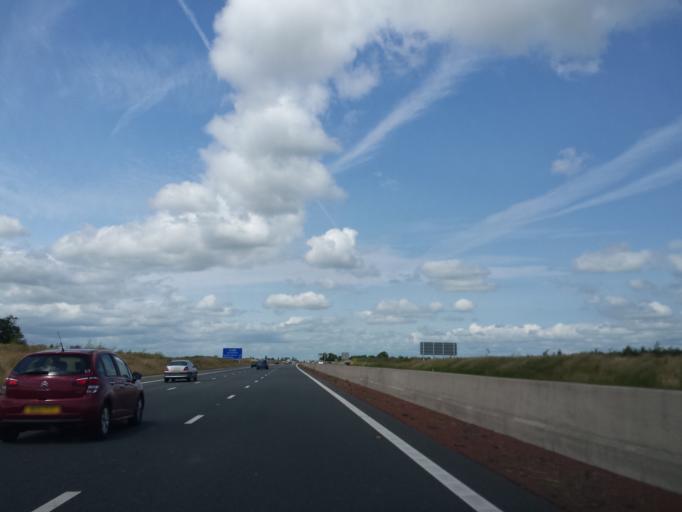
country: GB
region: England
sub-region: North Yorkshire
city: Ripon
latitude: 54.1976
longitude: -1.4686
